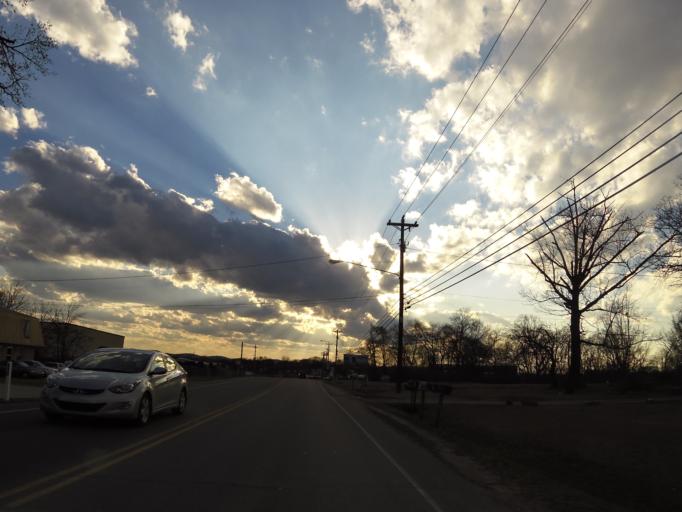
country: US
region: Tennessee
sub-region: Wilson County
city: Lebanon
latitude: 36.2109
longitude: -86.2735
